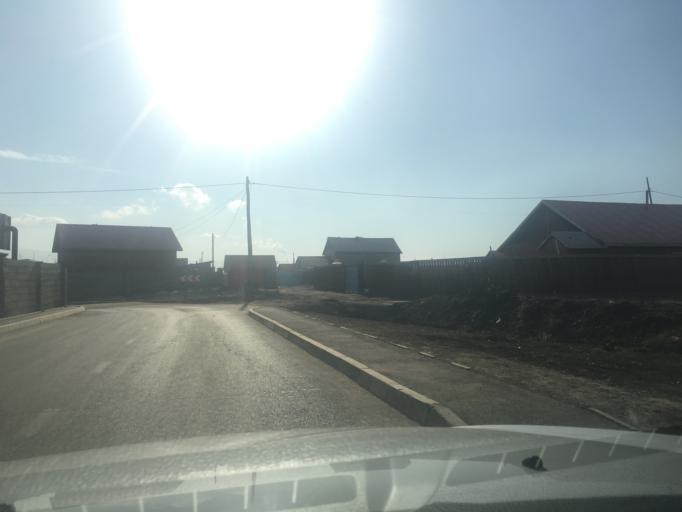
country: MN
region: Ulaanbaatar
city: Ulaanbaatar
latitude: 47.9657
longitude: 106.8270
